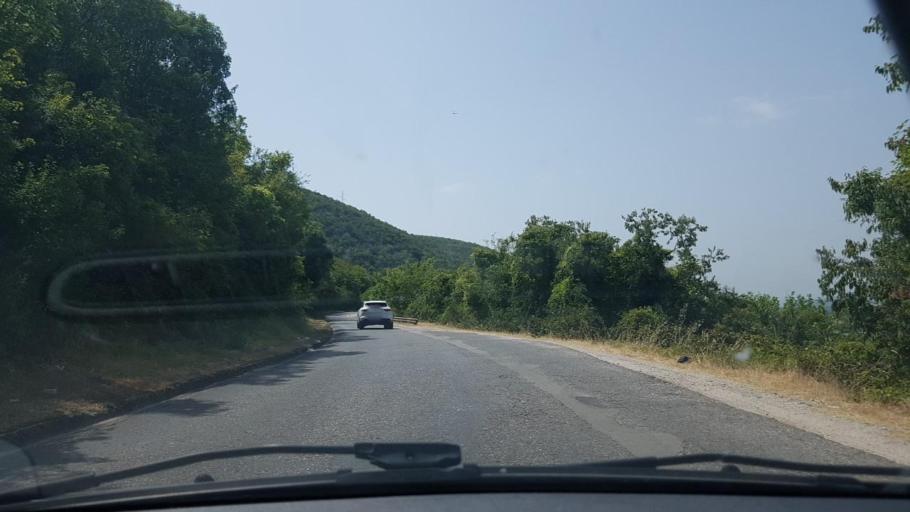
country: BA
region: Federation of Bosnia and Herzegovina
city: Tasovcici
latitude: 43.0282
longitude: 17.7507
